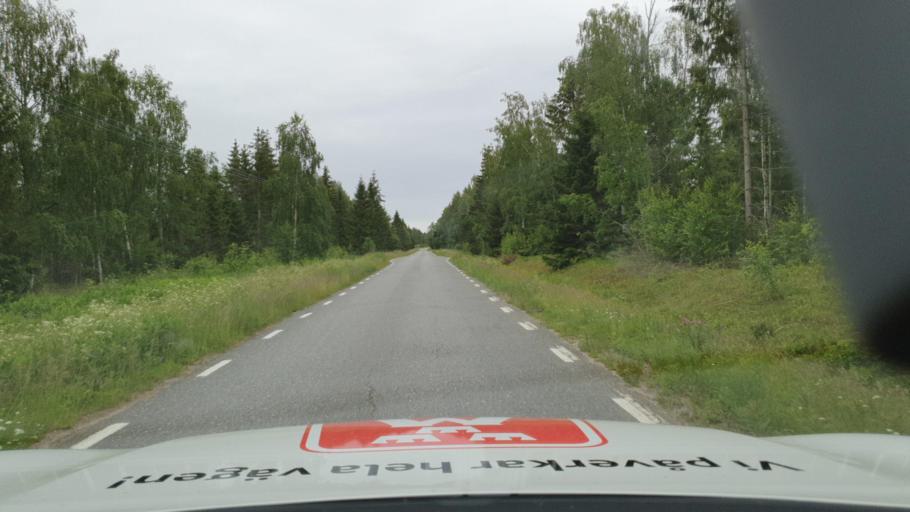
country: SE
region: Vaesterbotten
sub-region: Nordmalings Kommun
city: Nordmaling
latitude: 63.4638
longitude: 19.4655
